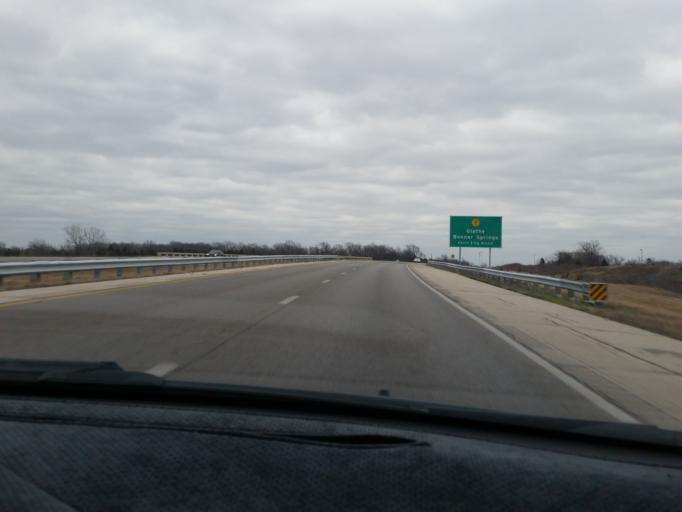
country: US
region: Kansas
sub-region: Johnson County
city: De Soto
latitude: 38.9477
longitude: -94.8871
